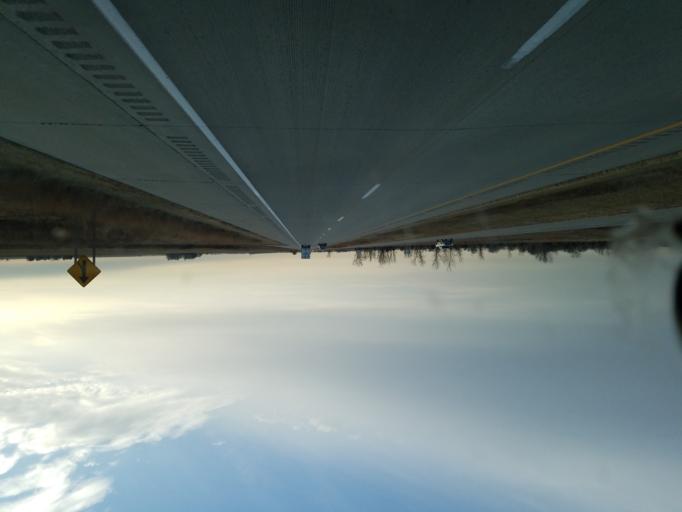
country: US
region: Iowa
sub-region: Monona County
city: Onawa
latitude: 41.9295
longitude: -96.1040
